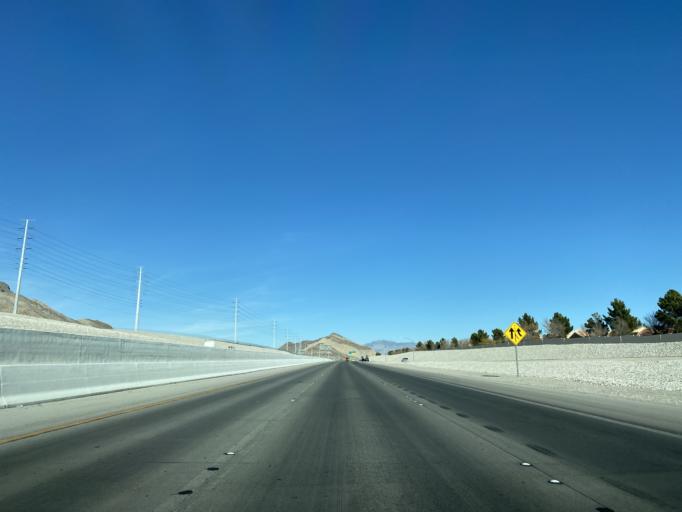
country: US
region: Nevada
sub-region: Clark County
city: Summerlin South
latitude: 36.1926
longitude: -115.3423
